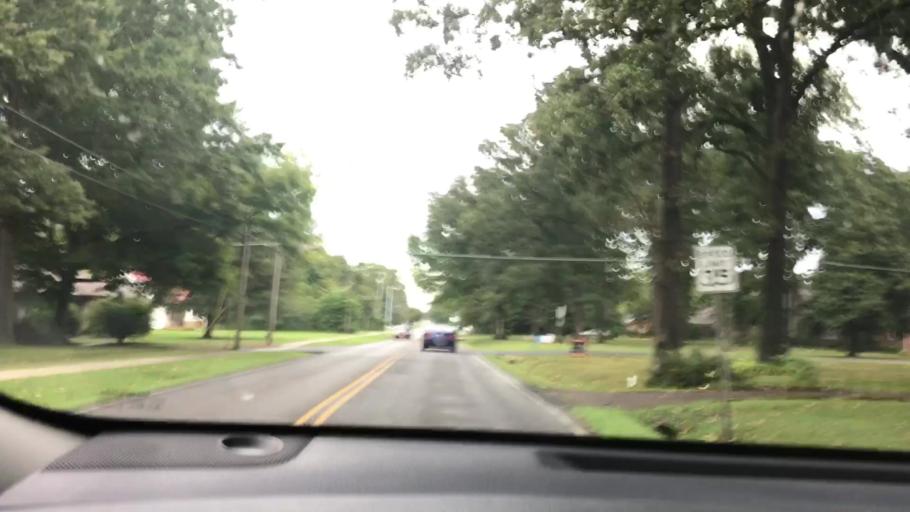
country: US
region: Kentucky
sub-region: Calloway County
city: Murray
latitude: 36.6028
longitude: -88.3135
